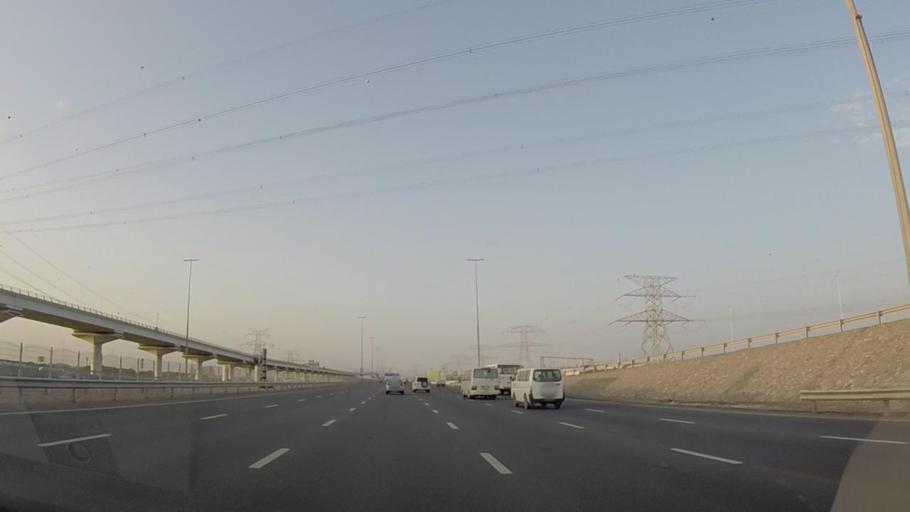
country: AE
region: Dubai
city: Dubai
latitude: 25.0328
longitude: 55.1045
